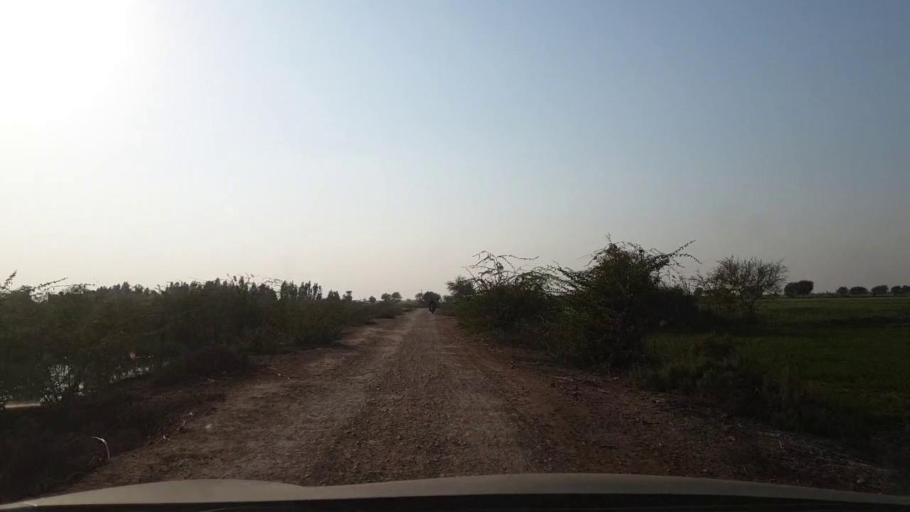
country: PK
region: Sindh
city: Berani
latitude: 25.6515
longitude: 68.8119
